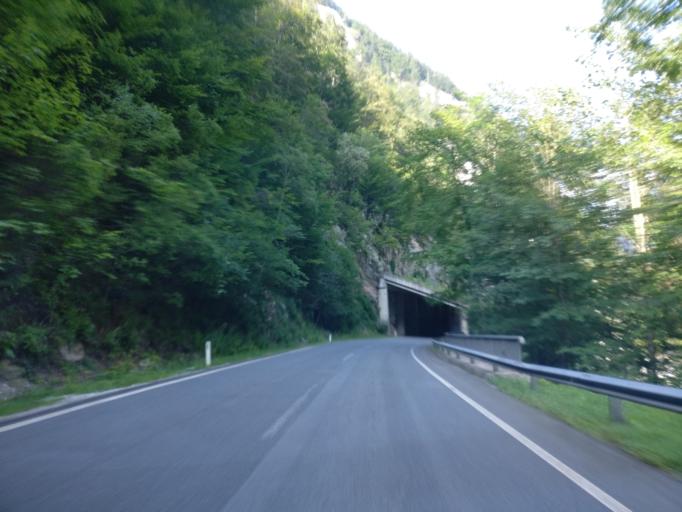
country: AT
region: Styria
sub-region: Politischer Bezirk Leoben
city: Hieflau
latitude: 47.5934
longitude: 14.7085
